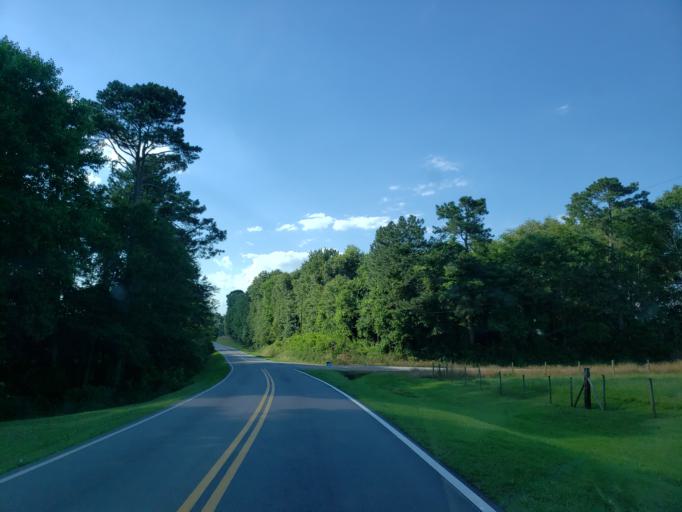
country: US
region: Georgia
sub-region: Haralson County
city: Bremen
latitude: 33.6632
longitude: -85.1127
